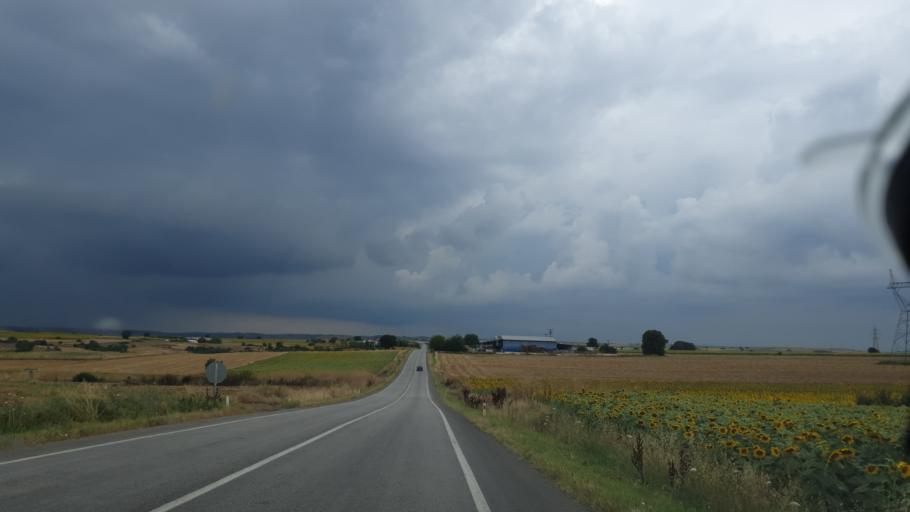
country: TR
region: Tekirdag
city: Hayrabolu
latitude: 41.2184
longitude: 27.0832
